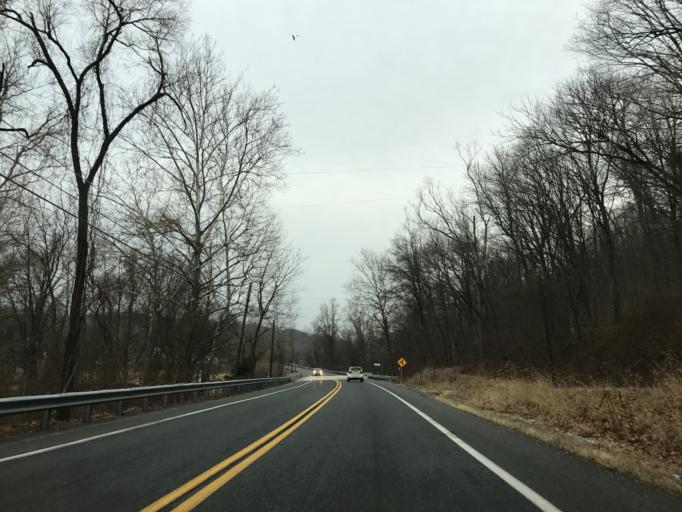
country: US
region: Pennsylvania
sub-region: Adams County
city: Carroll Valley
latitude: 39.7308
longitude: -77.3652
